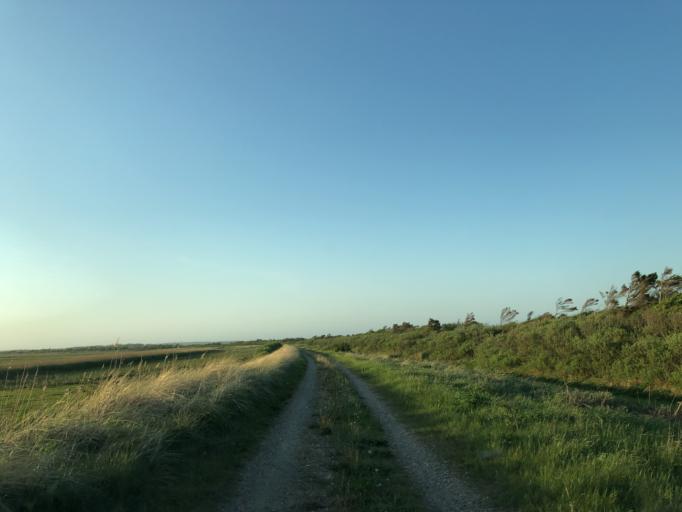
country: DK
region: Central Jutland
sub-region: Holstebro Kommune
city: Ulfborg
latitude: 56.2343
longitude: 8.1676
